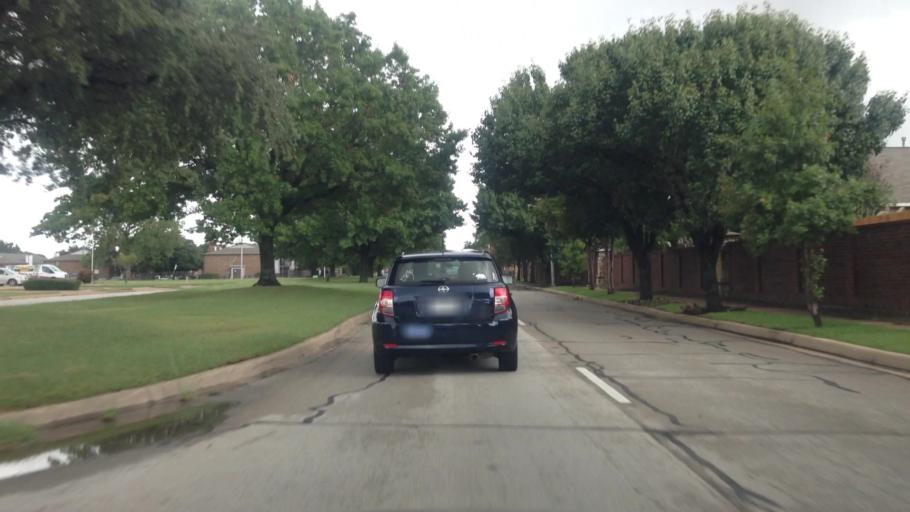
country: US
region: Texas
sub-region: Tarrant County
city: Edgecliff Village
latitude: 32.6370
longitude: -97.3941
